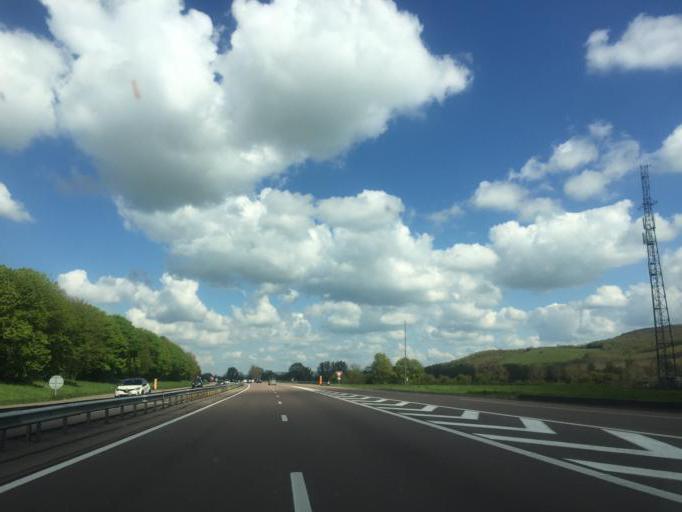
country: FR
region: Bourgogne
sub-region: Departement de la Cote-d'Or
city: Pouilly-en-Auxois
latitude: 47.3122
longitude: 4.4993
